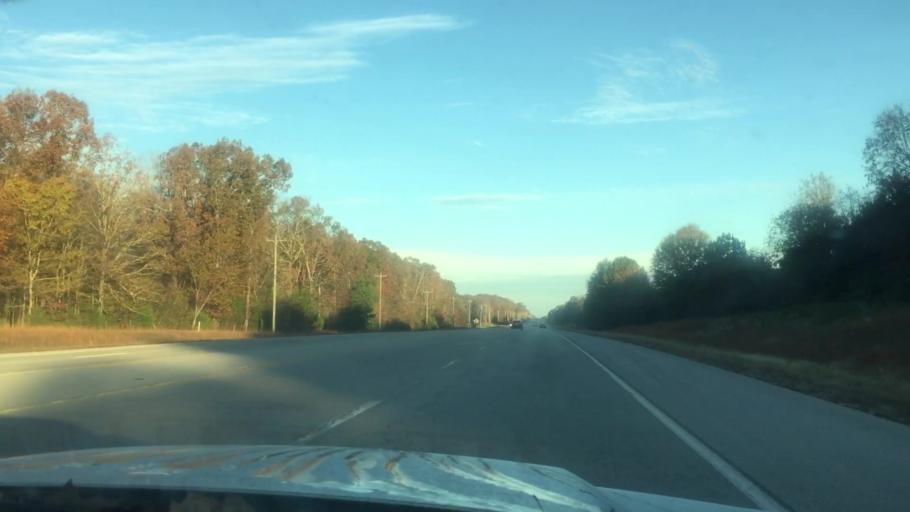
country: US
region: Tennessee
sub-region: Franklin County
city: Estill Springs
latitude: 35.3084
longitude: -86.1613
